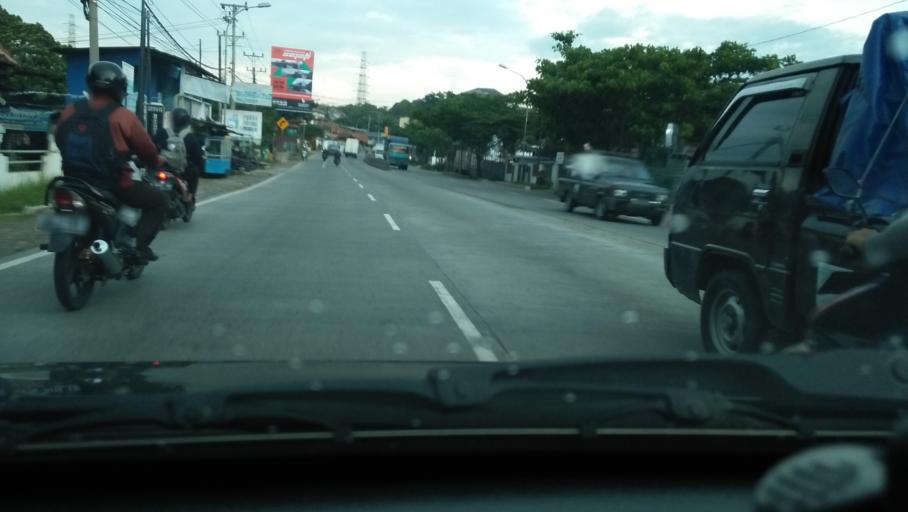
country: ID
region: Central Java
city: Ungaran
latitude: -7.0932
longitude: 110.4095
